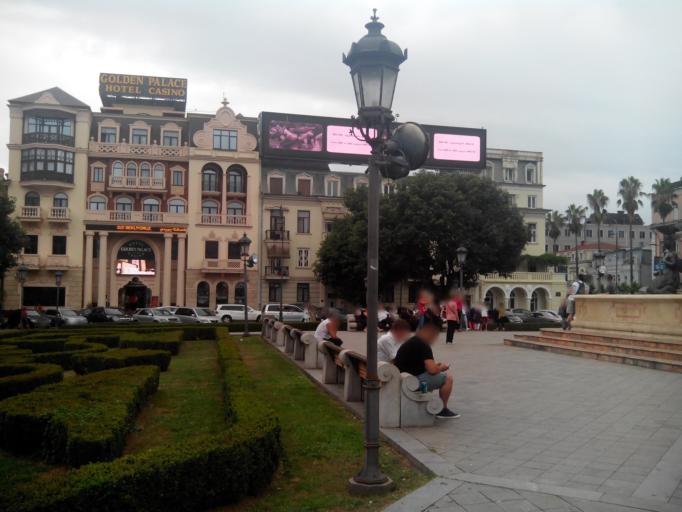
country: GE
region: Ajaria
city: Batumi
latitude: 41.6524
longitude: 41.6376
